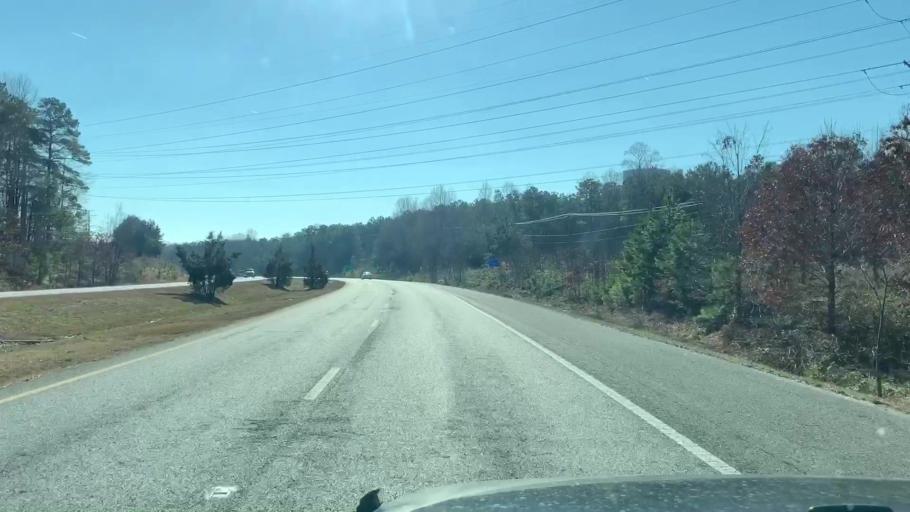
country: US
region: Virginia
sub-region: James City County
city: Williamsburg
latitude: 37.3274
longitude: -76.7559
